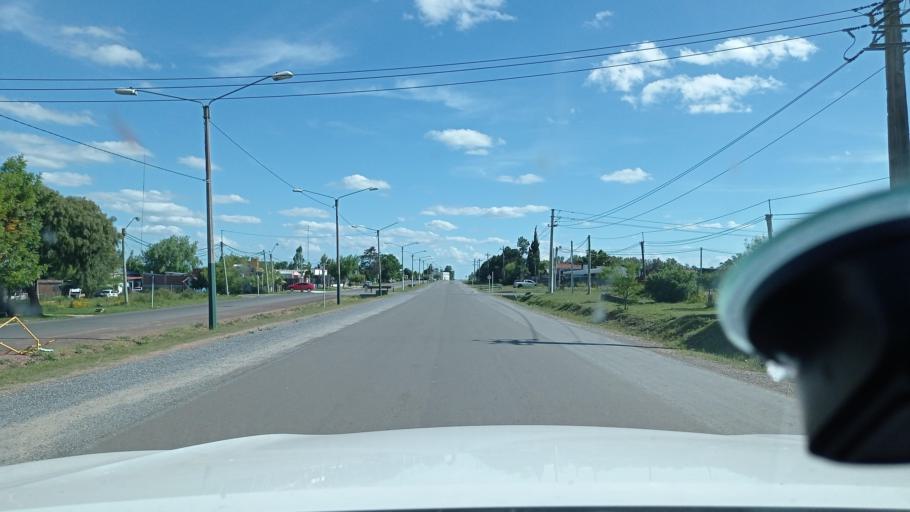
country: UY
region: Florida
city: Florida
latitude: -34.0875
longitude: -56.2377
